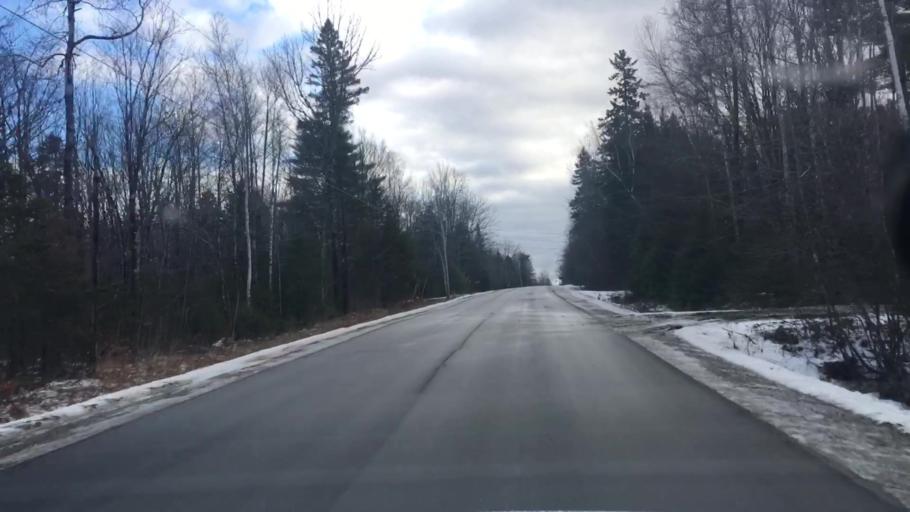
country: US
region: Maine
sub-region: Hancock County
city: Dedham
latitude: 44.6790
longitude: -68.7049
